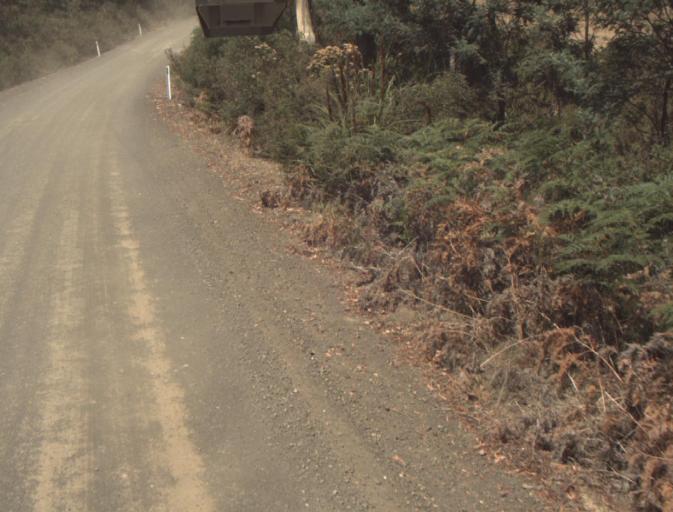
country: AU
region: Tasmania
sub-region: Launceston
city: Mayfield
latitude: -41.2749
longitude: 147.1071
